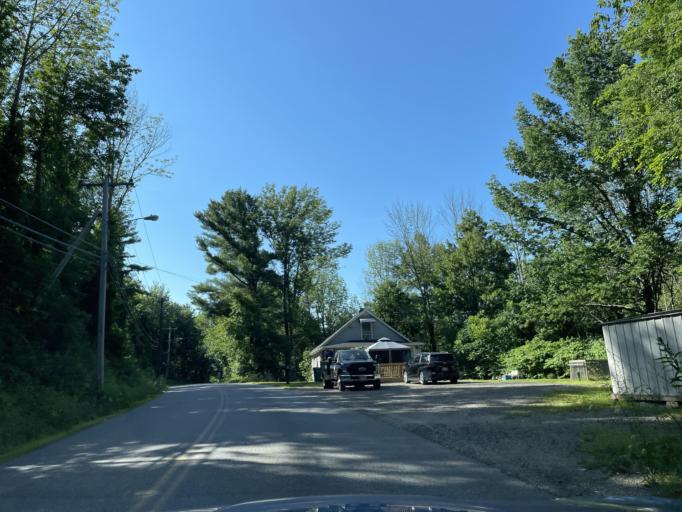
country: US
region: Massachusetts
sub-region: Worcester County
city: Charlton
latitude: 42.1501
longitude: -71.9903
